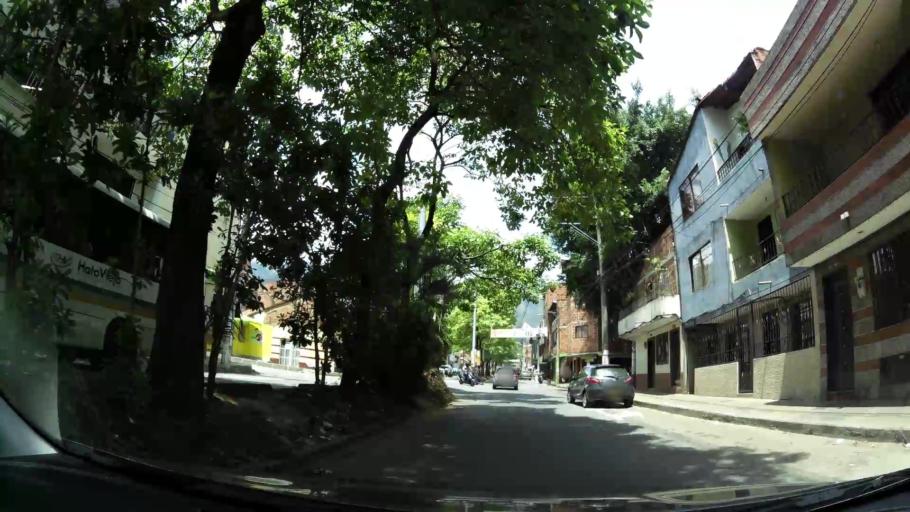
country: CO
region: Antioquia
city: Bello
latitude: 6.3389
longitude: -75.5614
